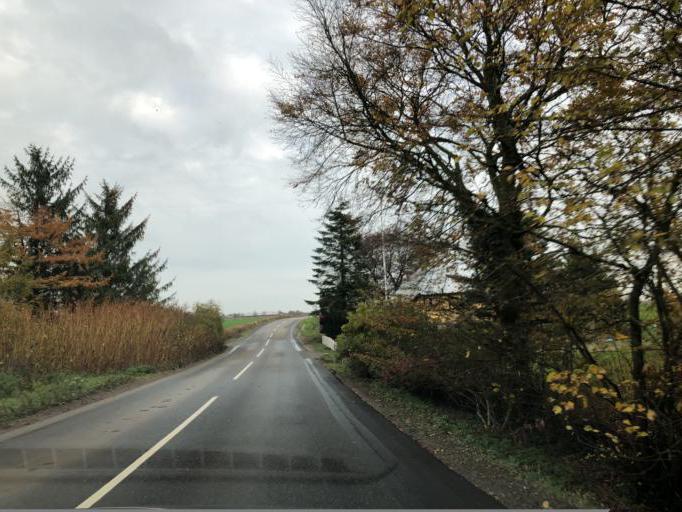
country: DK
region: Central Jutland
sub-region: Hedensted Kommune
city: Hornsyld
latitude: 55.7374
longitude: 9.7902
